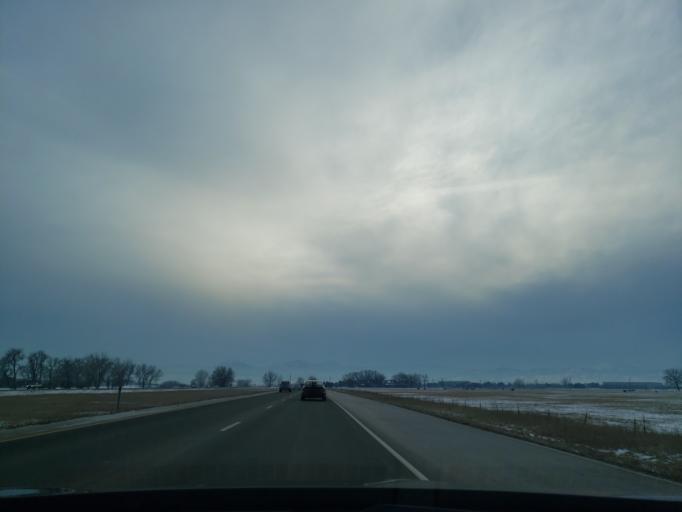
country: US
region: Colorado
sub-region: Boulder County
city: Niwot
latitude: 40.0979
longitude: -105.1818
